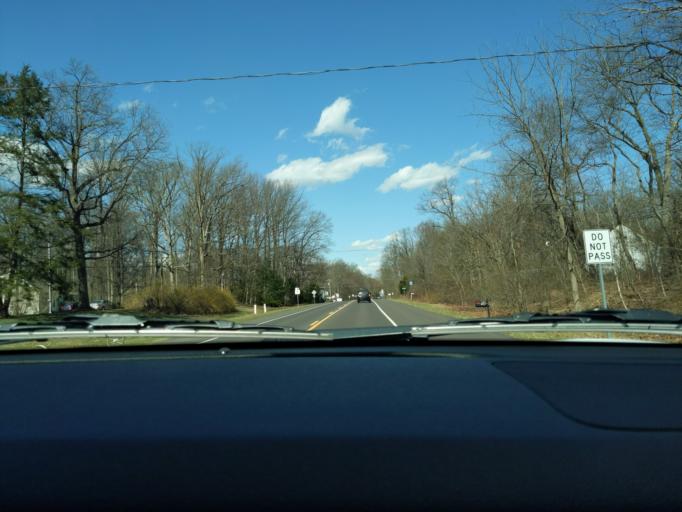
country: US
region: Pennsylvania
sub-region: Bucks County
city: Richlandtown
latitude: 40.4471
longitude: -75.2556
